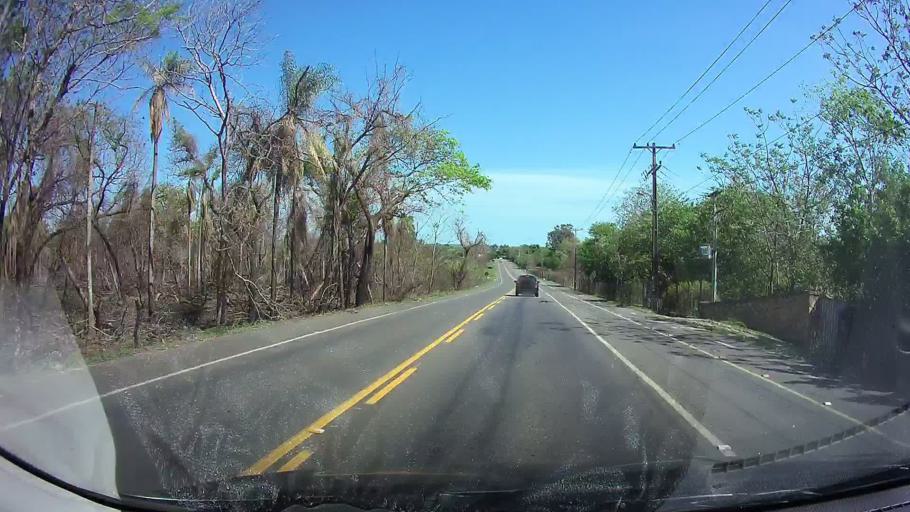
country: PY
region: Cordillera
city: San Bernardino
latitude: -25.2530
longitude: -57.3203
